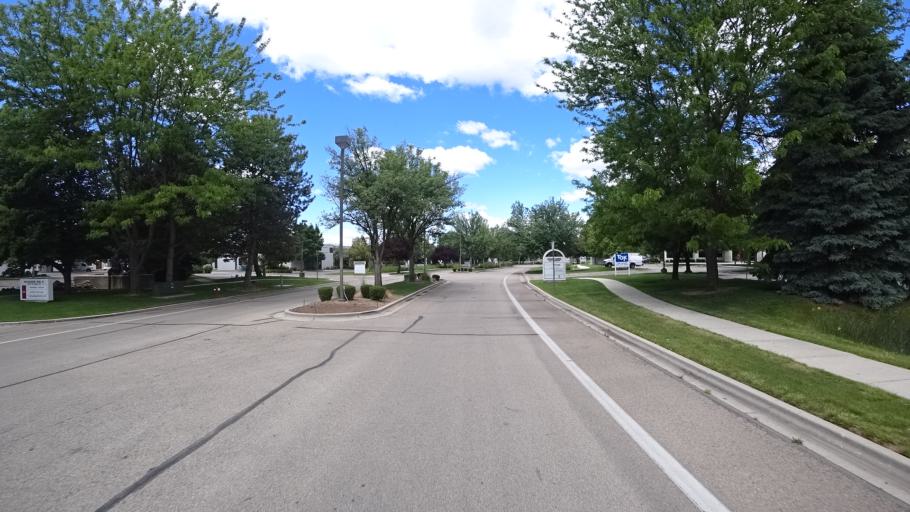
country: US
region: Idaho
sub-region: Ada County
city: Eagle
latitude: 43.6599
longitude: -116.3375
